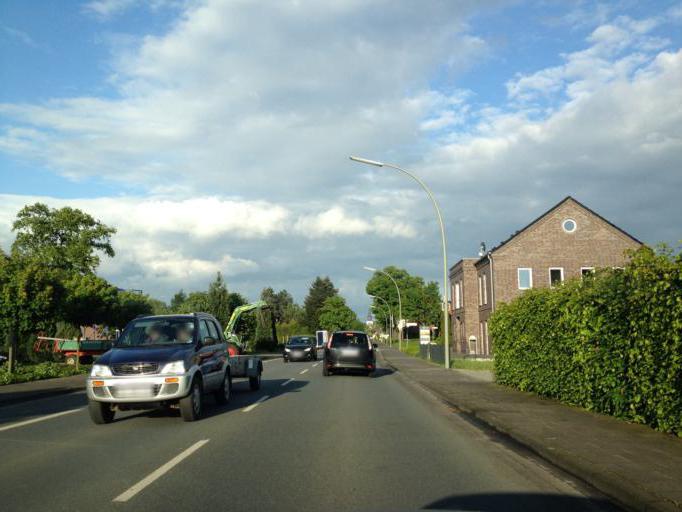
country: DE
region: North Rhine-Westphalia
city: Rietberg
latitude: 51.8154
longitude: 8.4840
